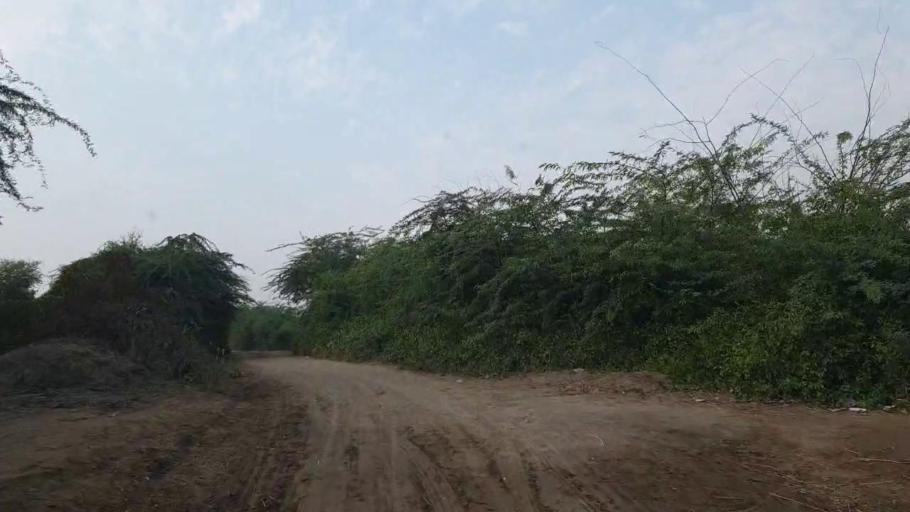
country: PK
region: Sindh
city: Tando Bago
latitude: 24.7788
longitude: 68.8751
